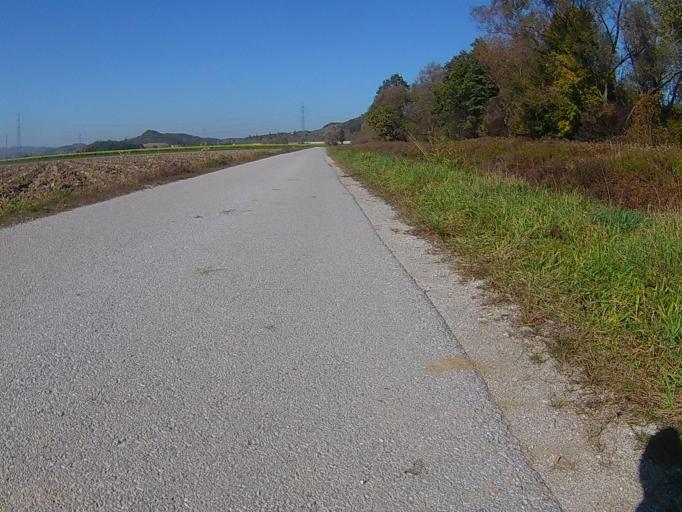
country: SI
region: Pesnica
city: Pesnica pri Mariboru
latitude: 46.5826
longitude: 15.7232
